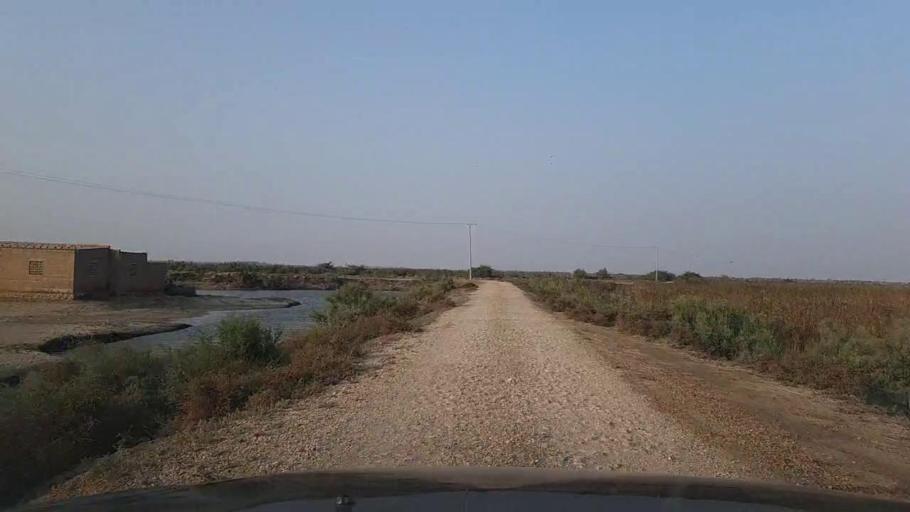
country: PK
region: Sindh
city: Mirpur Sakro
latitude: 24.4142
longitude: 67.7322
